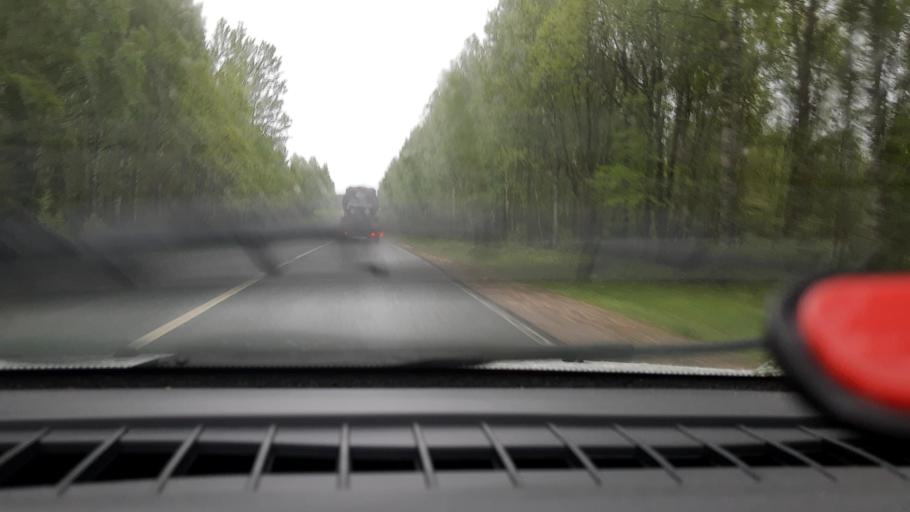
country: RU
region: Nizjnij Novgorod
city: Sukhobezvodnoye
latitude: 56.8668
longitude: 44.9248
